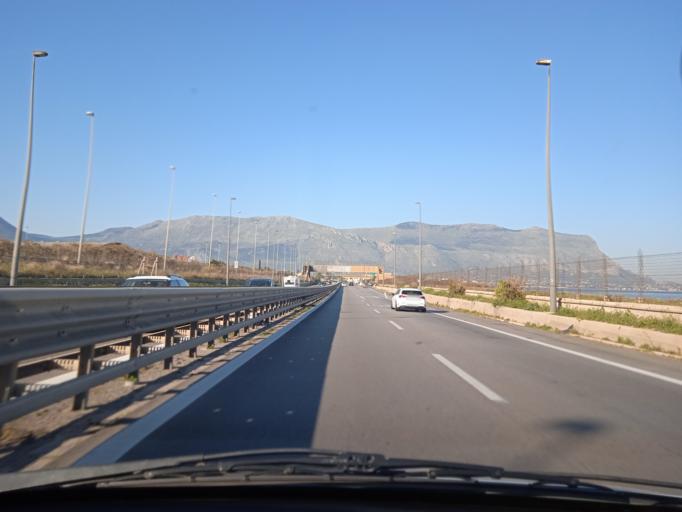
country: IT
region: Sicily
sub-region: Palermo
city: Capaci
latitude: 38.1770
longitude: 13.2209
